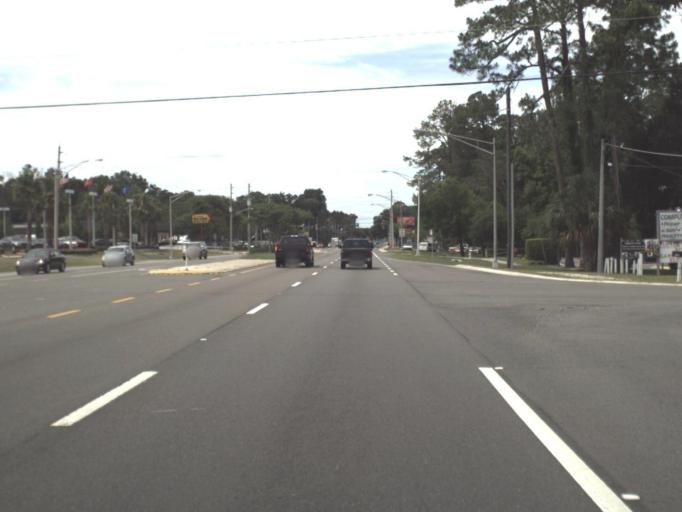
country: US
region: Florida
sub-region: Clay County
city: Bellair-Meadowbrook Terrace
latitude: 30.2241
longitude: -81.7375
